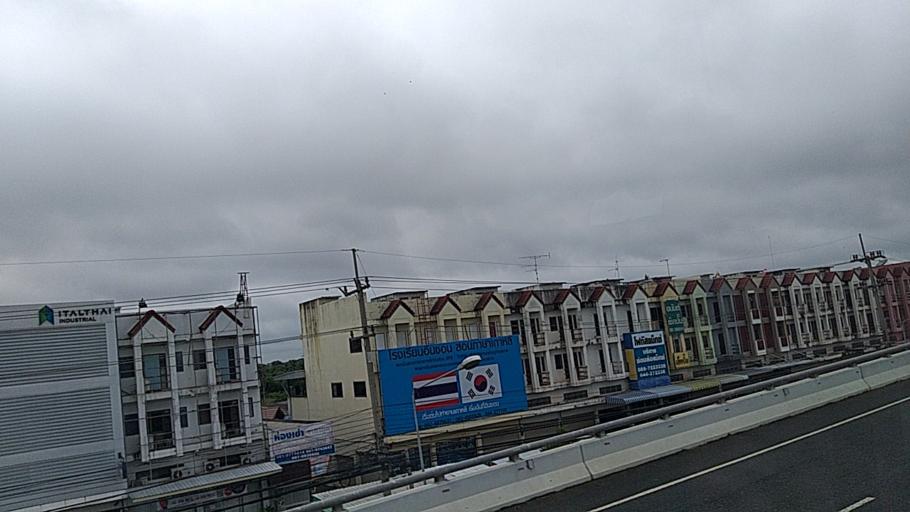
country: TH
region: Nakhon Ratchasima
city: Nakhon Ratchasima
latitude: 15.0264
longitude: 102.1377
